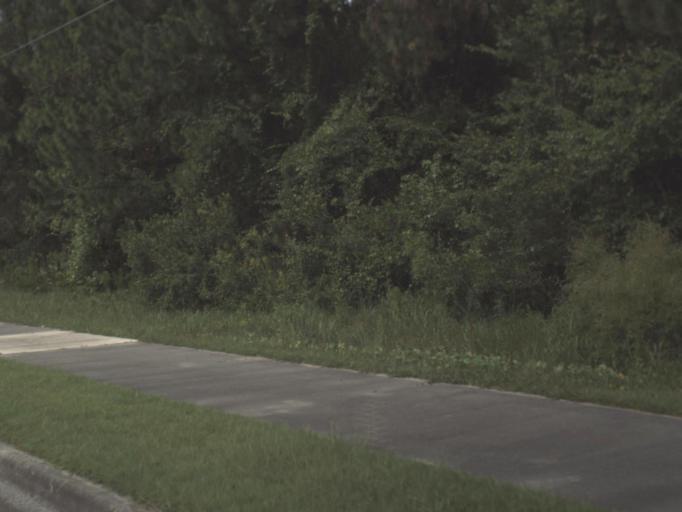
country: US
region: Florida
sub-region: Columbia County
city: Five Points
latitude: 30.2387
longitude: -82.6387
